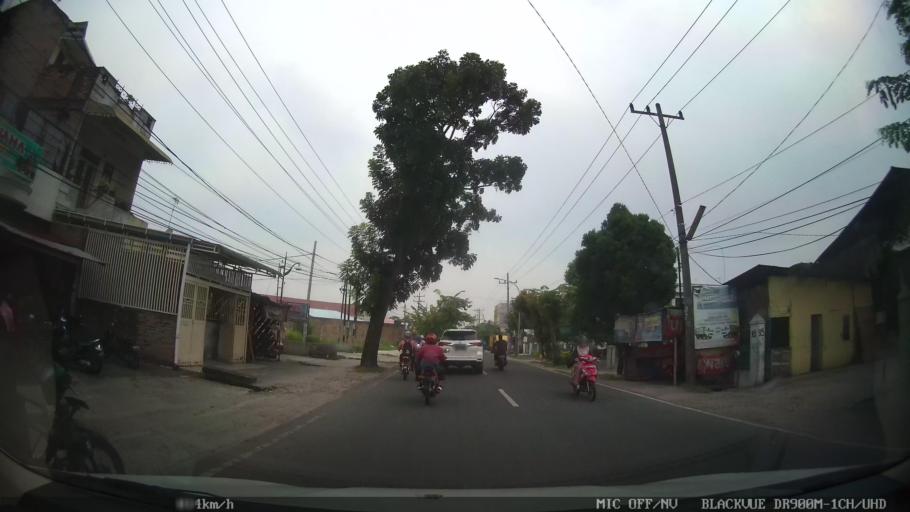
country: ID
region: North Sumatra
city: Medan
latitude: 3.5637
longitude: 98.7217
